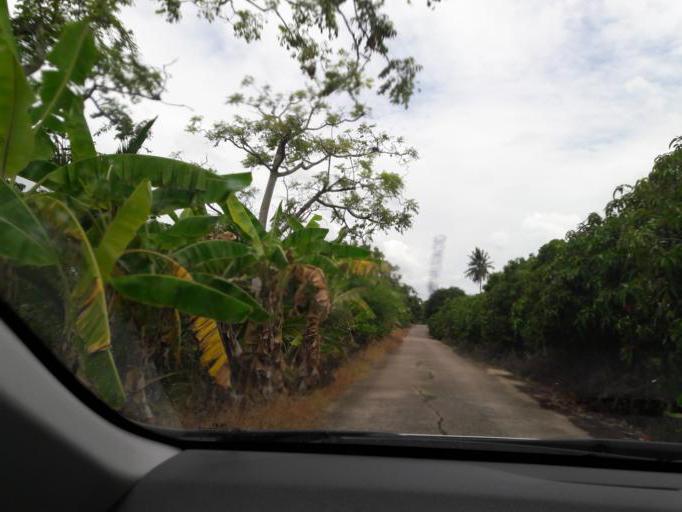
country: TH
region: Ratchaburi
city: Damnoen Saduak
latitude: 13.5480
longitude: 100.0075
